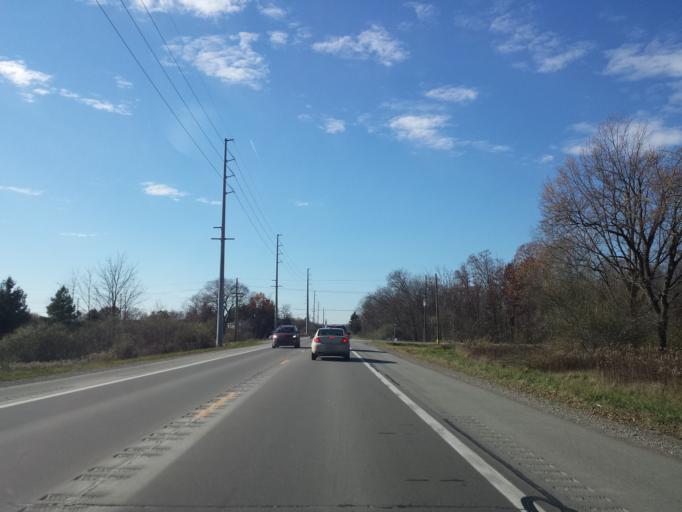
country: US
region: Michigan
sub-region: Livingston County
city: Brighton
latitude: 42.6309
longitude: -83.8058
